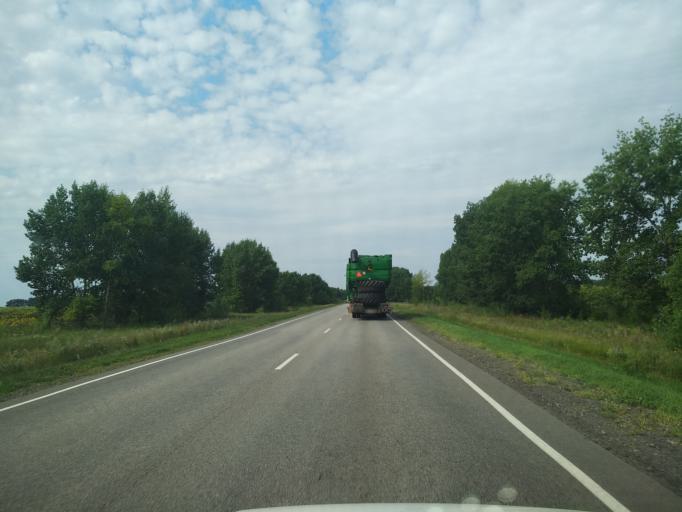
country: RU
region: Voronezj
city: Pereleshinskiy
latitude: 51.8711
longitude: 40.3900
